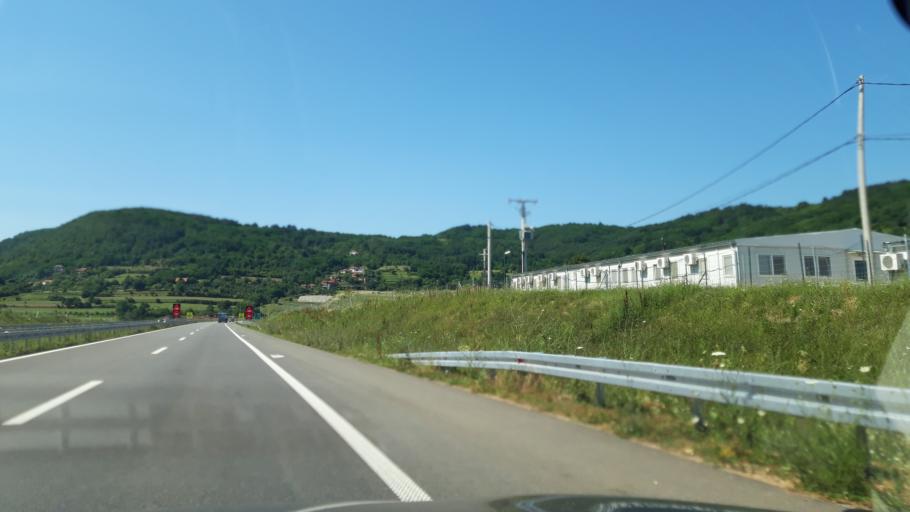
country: RS
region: Central Serbia
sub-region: Pcinjski Okrug
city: Vladicin Han
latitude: 42.7249
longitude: 22.0755
